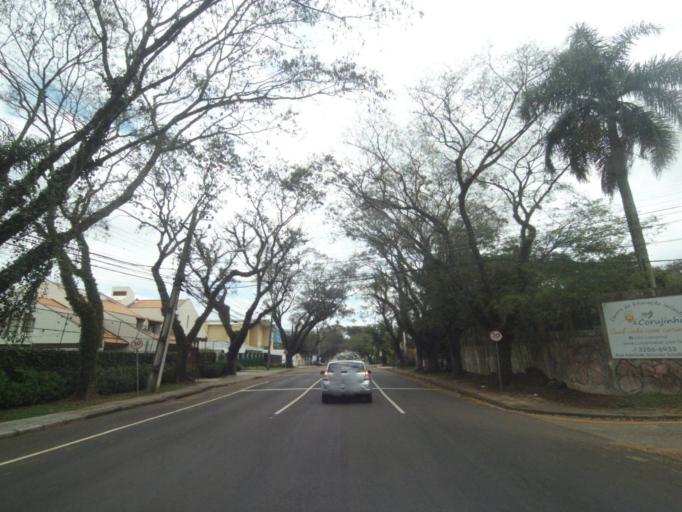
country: BR
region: Parana
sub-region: Curitiba
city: Curitiba
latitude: -25.4116
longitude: -49.2352
